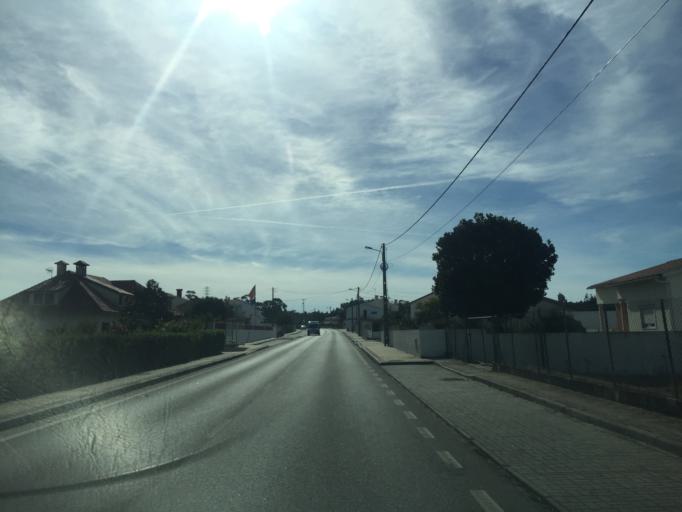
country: PT
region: Coimbra
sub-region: Figueira da Foz
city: Lavos
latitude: 40.0879
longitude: -8.8268
